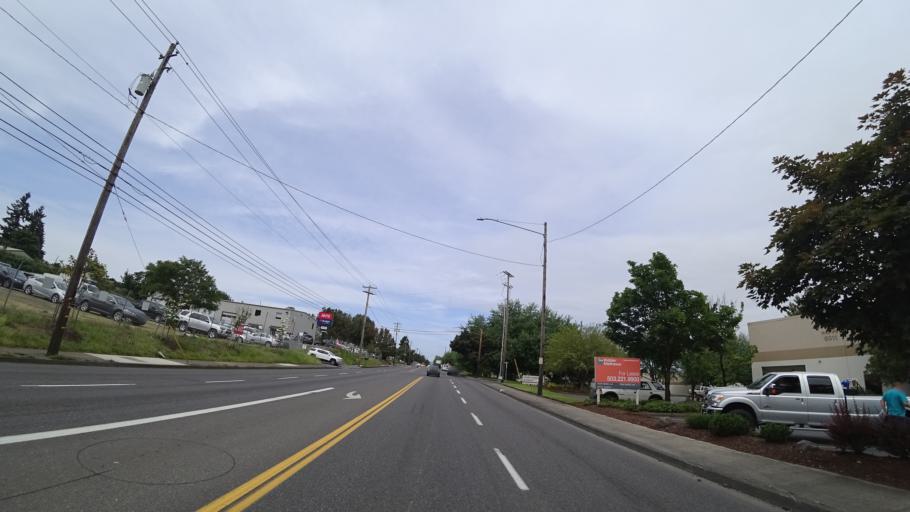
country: US
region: Oregon
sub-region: Multnomah County
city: Portland
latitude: 45.5688
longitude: -122.6007
